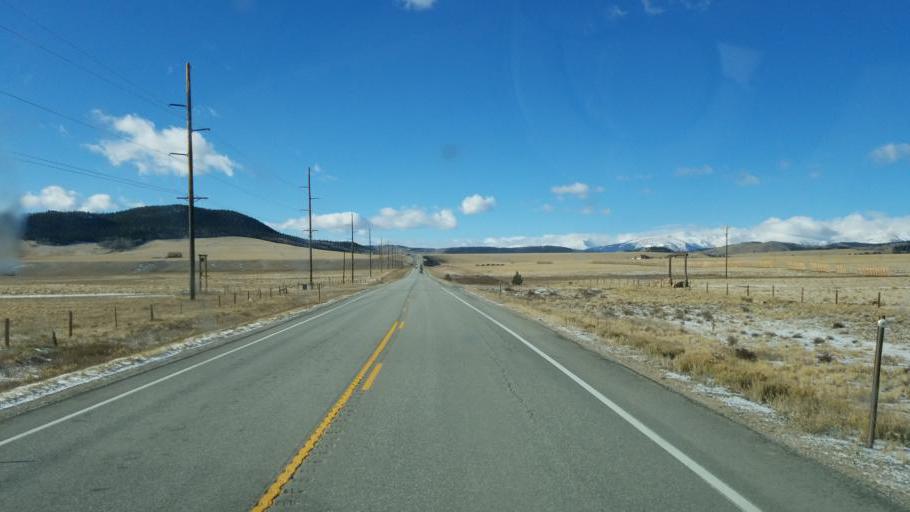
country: US
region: Colorado
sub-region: Park County
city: Fairplay
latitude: 39.2965
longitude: -105.9017
